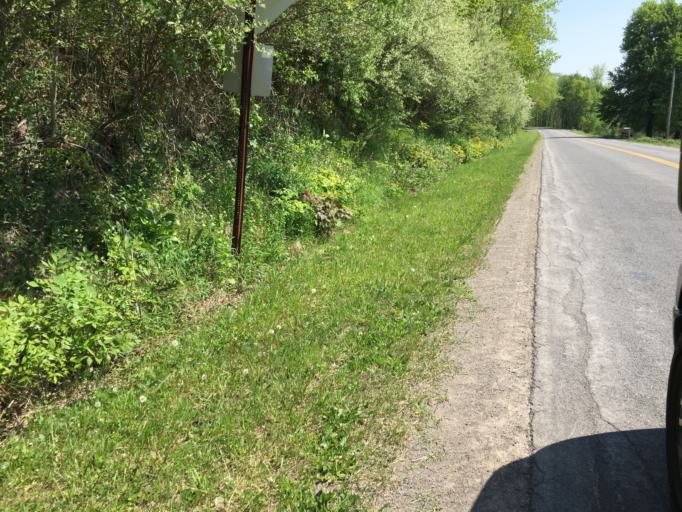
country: US
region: New York
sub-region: Wayne County
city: Marion
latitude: 43.1294
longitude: -77.1737
